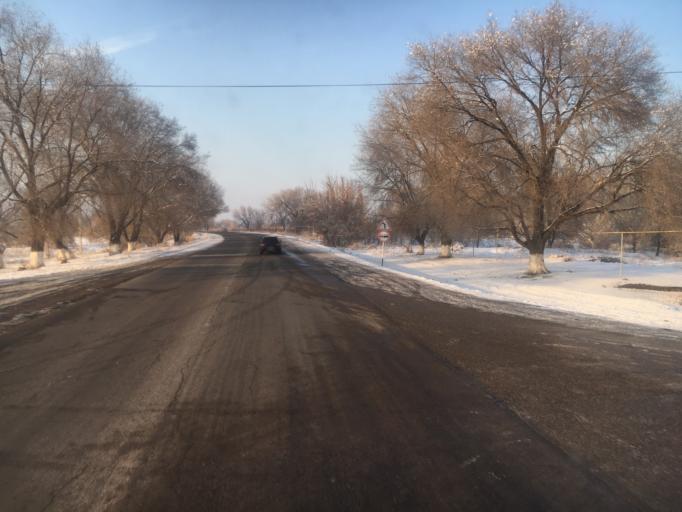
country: KZ
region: Almaty Oblysy
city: Burunday
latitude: 43.3396
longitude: 76.6589
